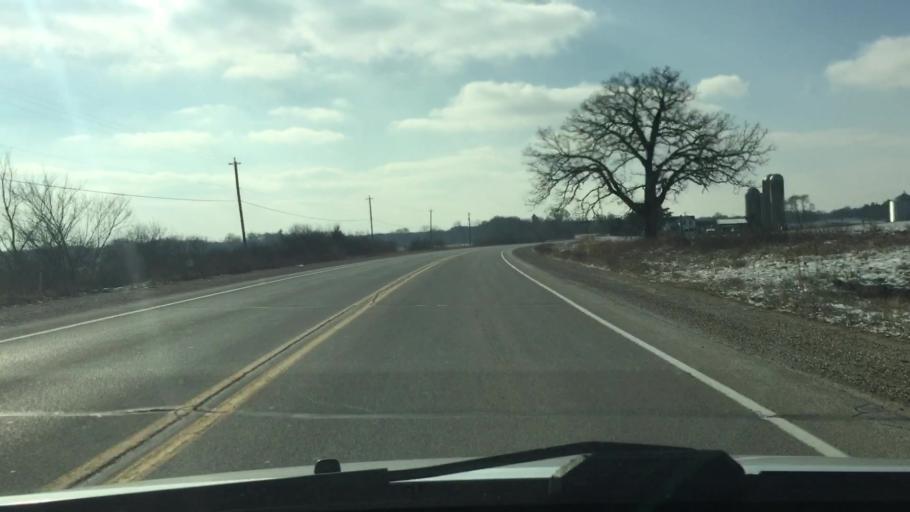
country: US
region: Wisconsin
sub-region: Waukesha County
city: North Prairie
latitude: 42.9256
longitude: -88.4292
